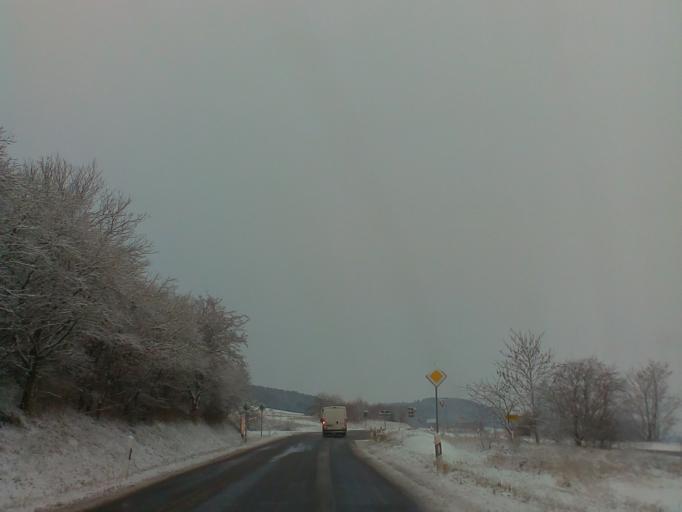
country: DE
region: Thuringia
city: Arnstadt
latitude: 50.8396
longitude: 10.9232
